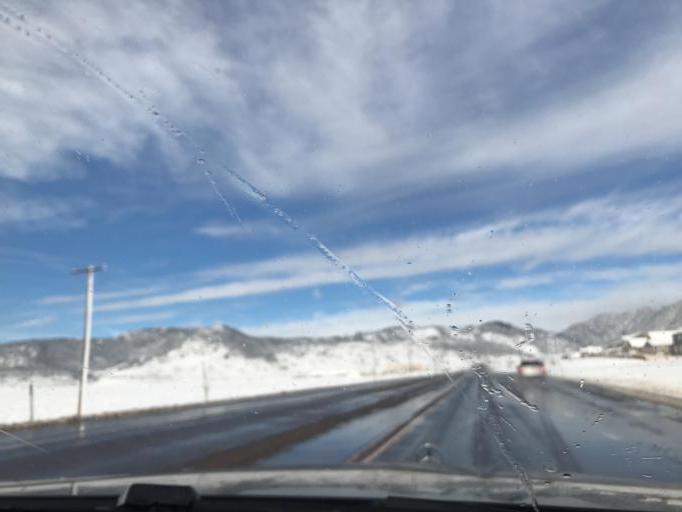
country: US
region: Colorado
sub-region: Boulder County
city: Superior
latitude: 39.8647
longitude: -105.2228
